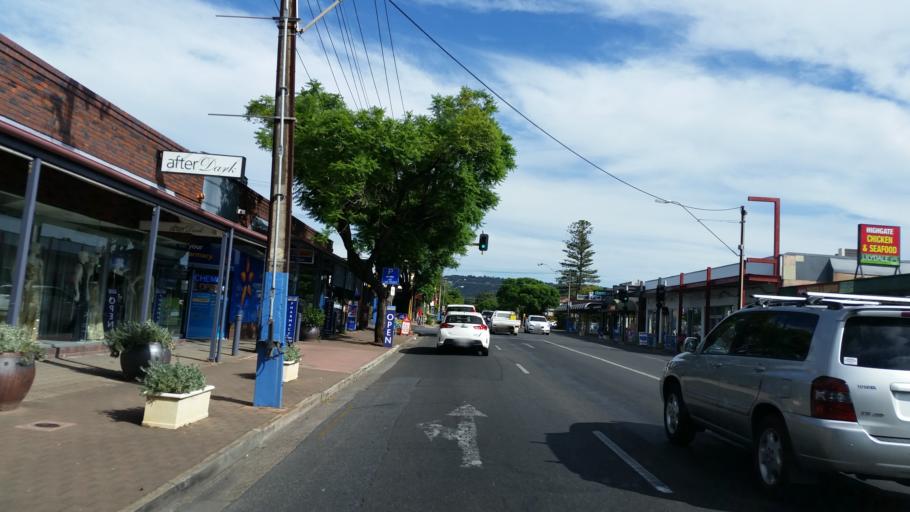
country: AU
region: South Australia
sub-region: Unley
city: Fullarton
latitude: -34.9600
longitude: 138.6262
